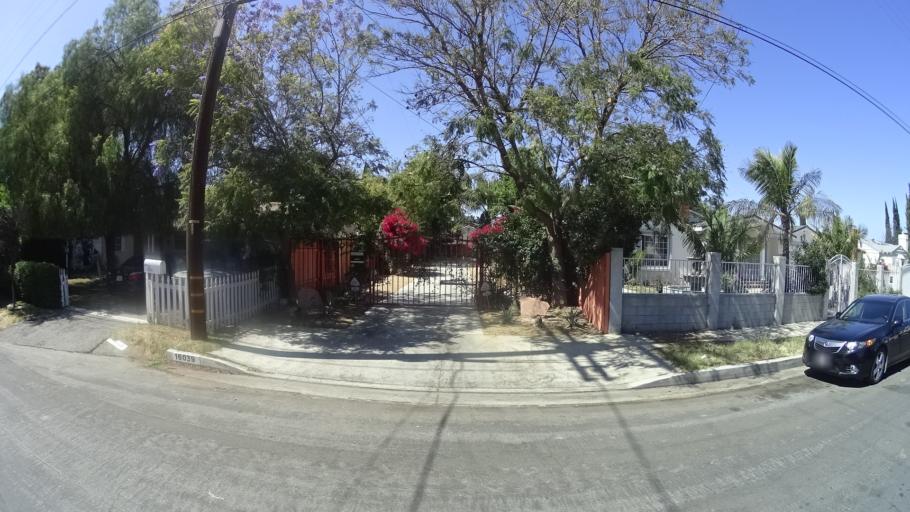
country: US
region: California
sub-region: Los Angeles County
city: Van Nuys
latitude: 34.1974
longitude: -118.4830
